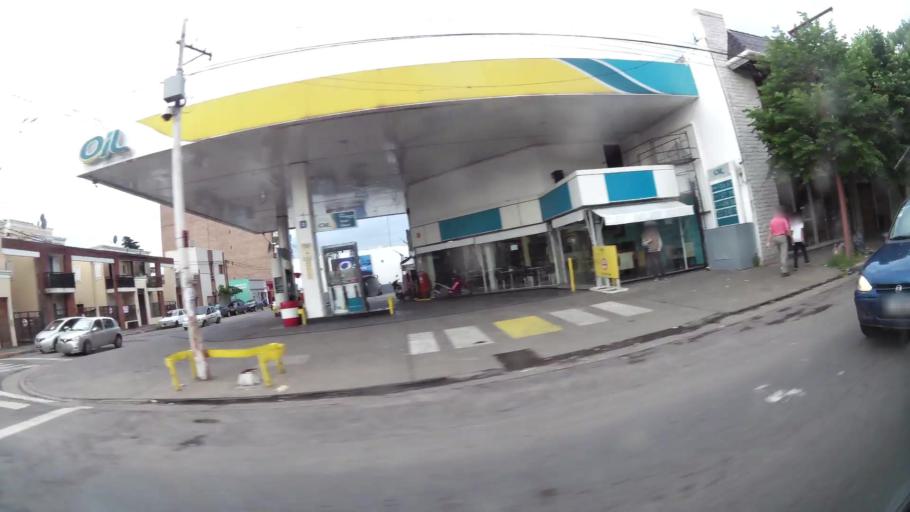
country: AR
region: Buenos Aires
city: San Nicolas de los Arroyos
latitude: -33.3396
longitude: -60.2179
